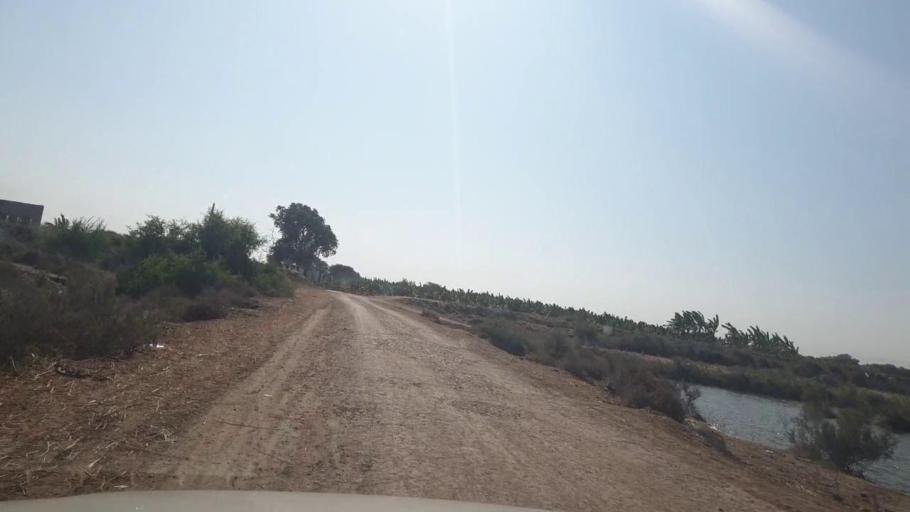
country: PK
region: Sindh
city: Chuhar Jamali
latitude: 24.4512
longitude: 67.8631
